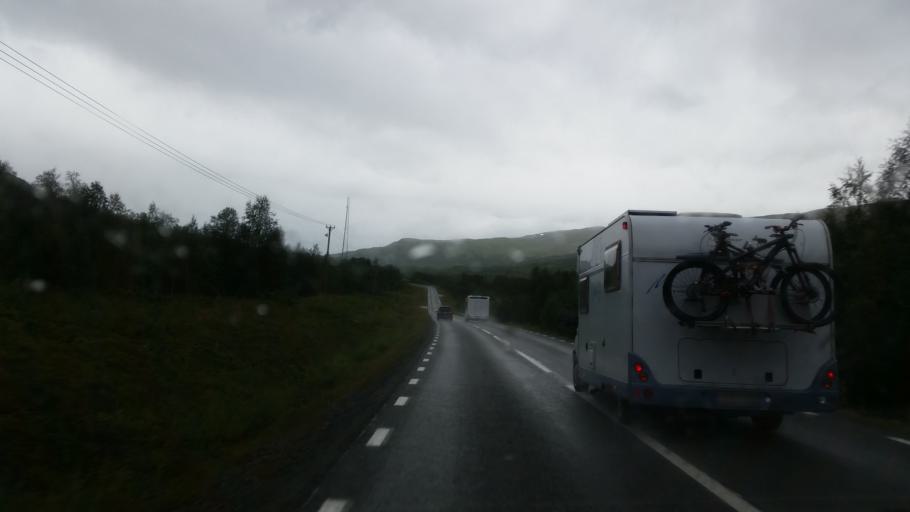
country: NO
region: Nordland
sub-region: Rana
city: Mo i Rana
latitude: 65.9163
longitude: 14.9956
